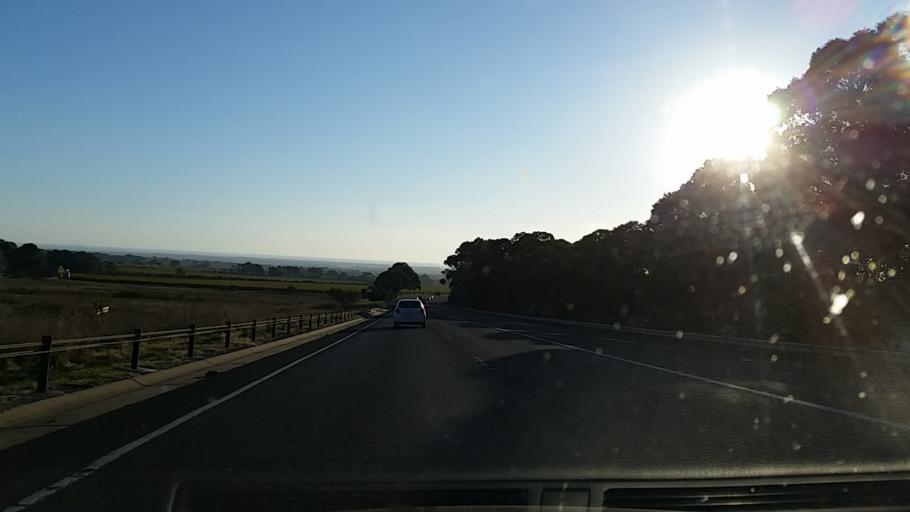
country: AU
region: South Australia
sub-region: Onkaparinga
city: McLaren Vale
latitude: -35.2785
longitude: 138.5521
